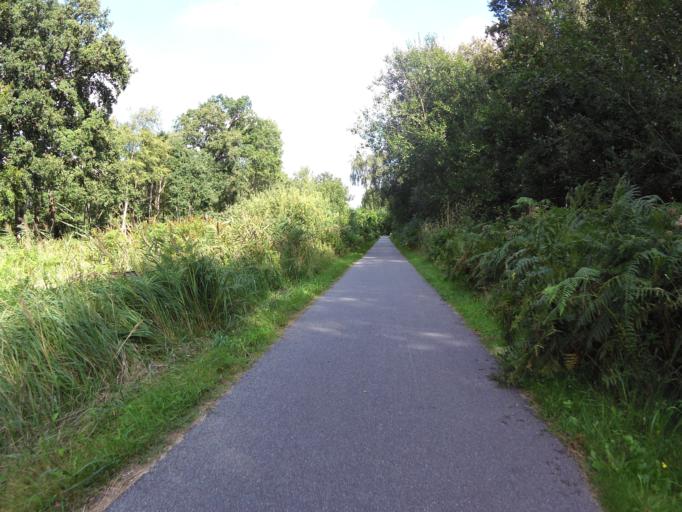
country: DE
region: Mecklenburg-Vorpommern
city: Karlshagen
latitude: 54.1433
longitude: 13.7963
